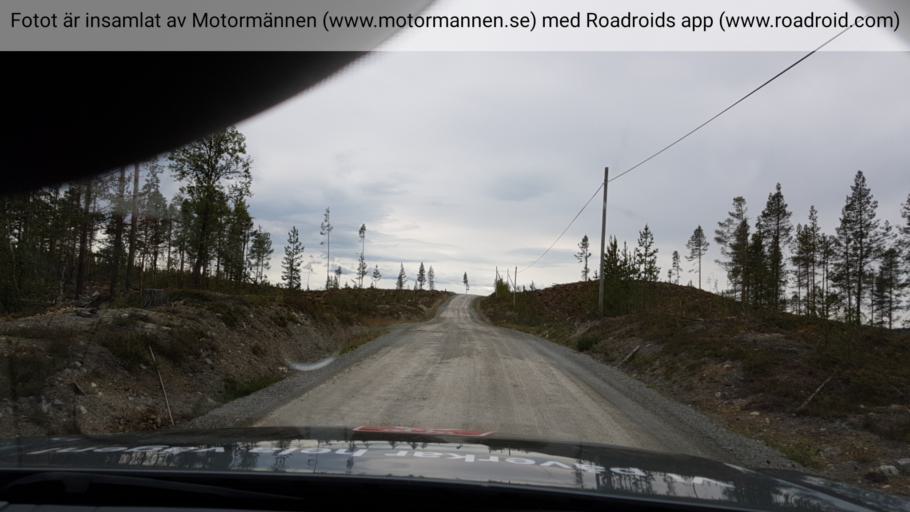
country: SE
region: Jaemtland
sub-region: Are Kommun
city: Jarpen
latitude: 62.8070
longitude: 13.8038
